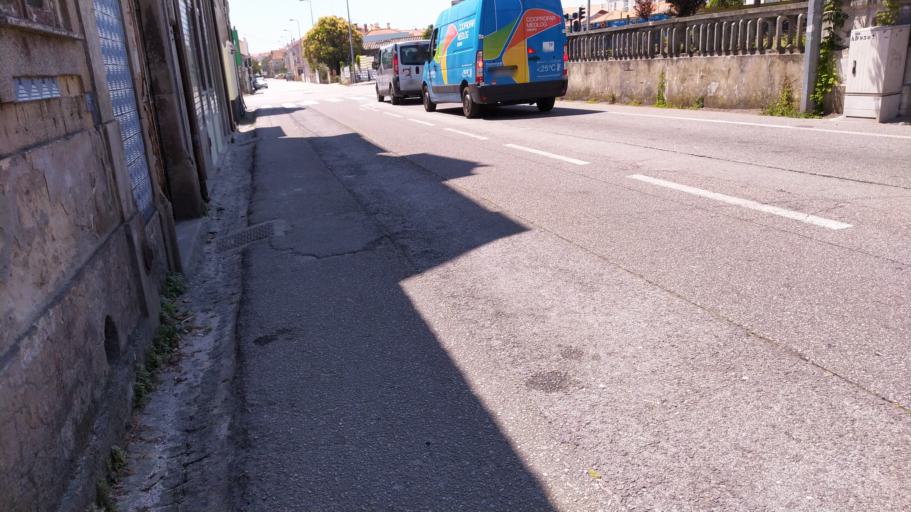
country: PT
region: Aveiro
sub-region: Aveiro
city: Aveiro
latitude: 40.6473
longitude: -8.6341
